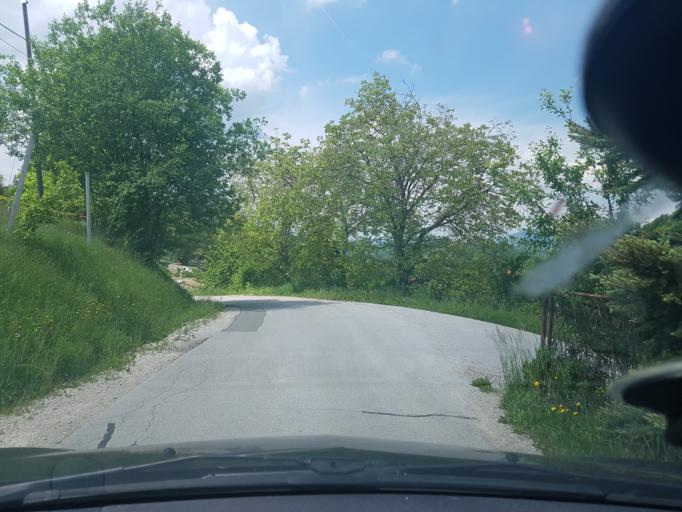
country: SI
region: Rogatec
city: Rogatec
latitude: 46.2125
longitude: 15.6950
